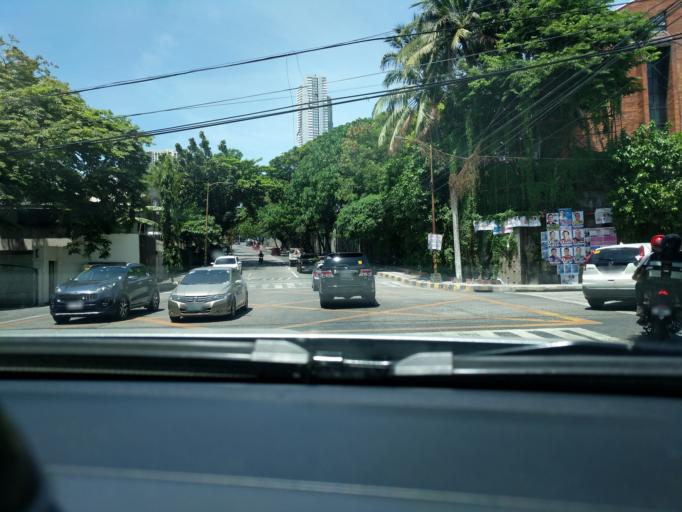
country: PH
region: Metro Manila
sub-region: Pasig
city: Pasig City
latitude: 14.5795
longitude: 121.0690
